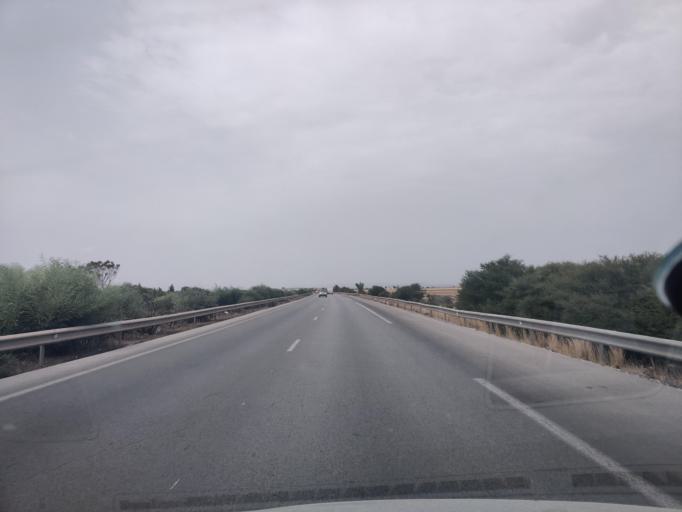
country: TN
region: Susah
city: Harqalah
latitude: 36.0304
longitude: 10.4244
